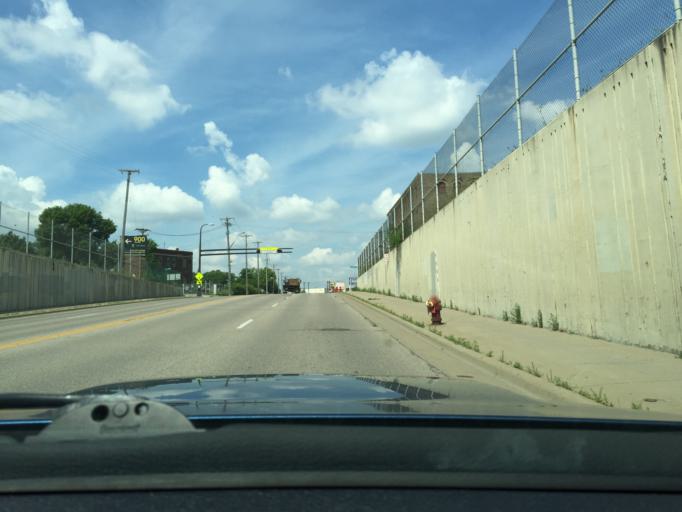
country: US
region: Minnesota
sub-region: Hennepin County
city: Minneapolis
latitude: 44.9915
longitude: -93.2424
